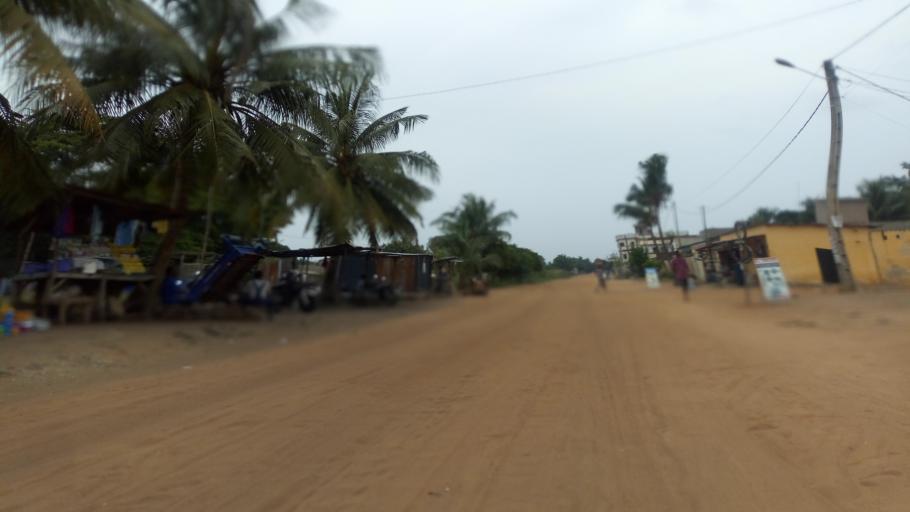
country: TG
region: Maritime
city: Lome
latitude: 6.1820
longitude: 1.1830
